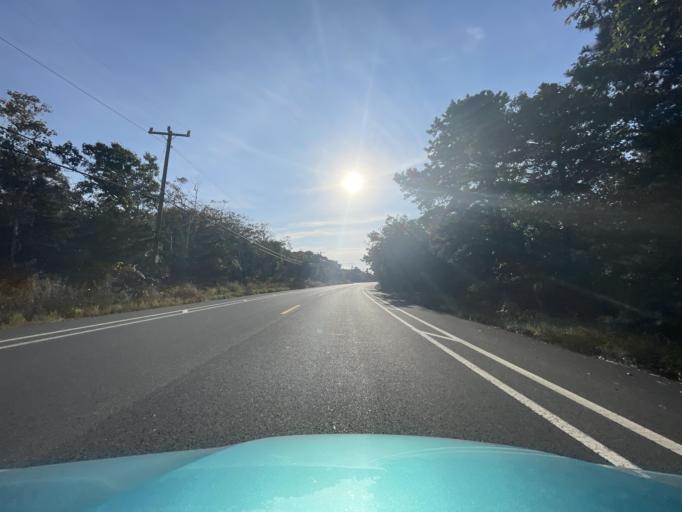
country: US
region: Massachusetts
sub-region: Bristol County
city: Head of Westport
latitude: 41.5065
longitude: -71.0449
